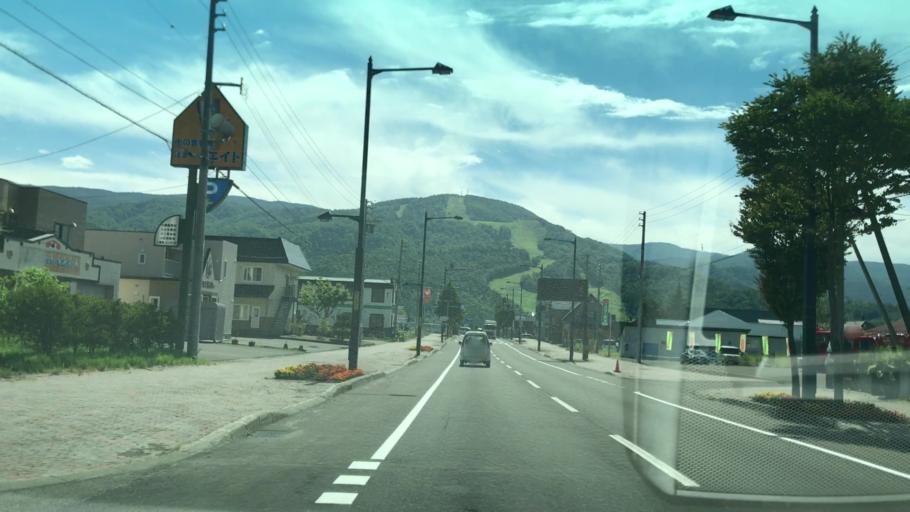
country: JP
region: Hokkaido
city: Shimo-furano
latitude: 42.8788
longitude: 142.4389
